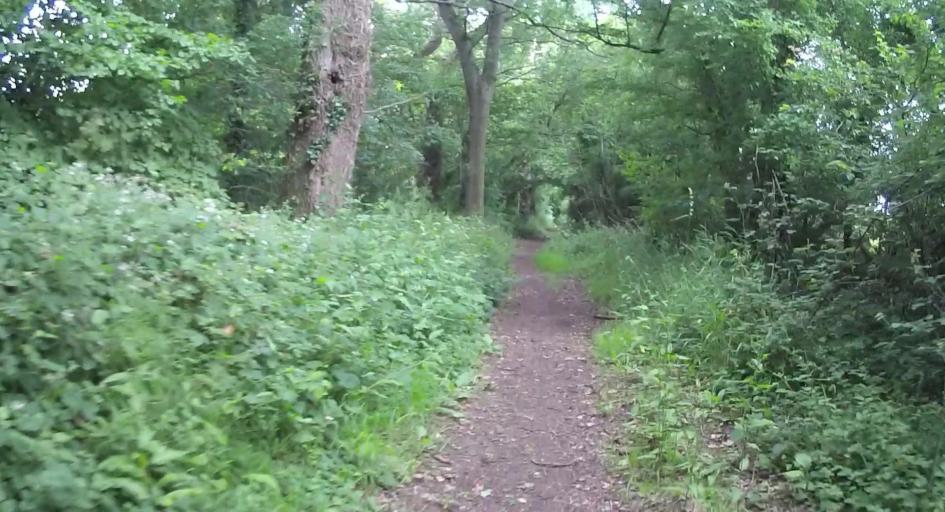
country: GB
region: England
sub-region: Hampshire
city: Basingstoke
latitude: 51.1672
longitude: -1.1651
